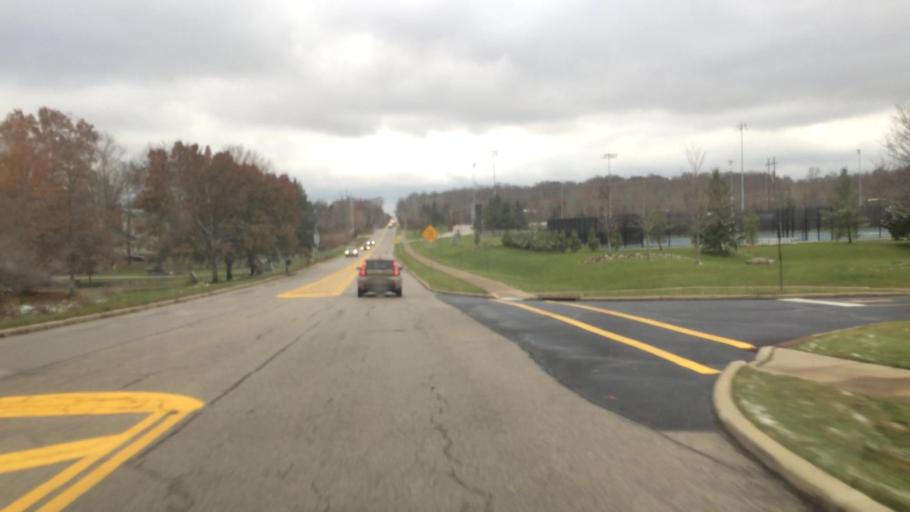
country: US
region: Ohio
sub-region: Summit County
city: Hudson
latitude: 41.2565
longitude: -81.4111
